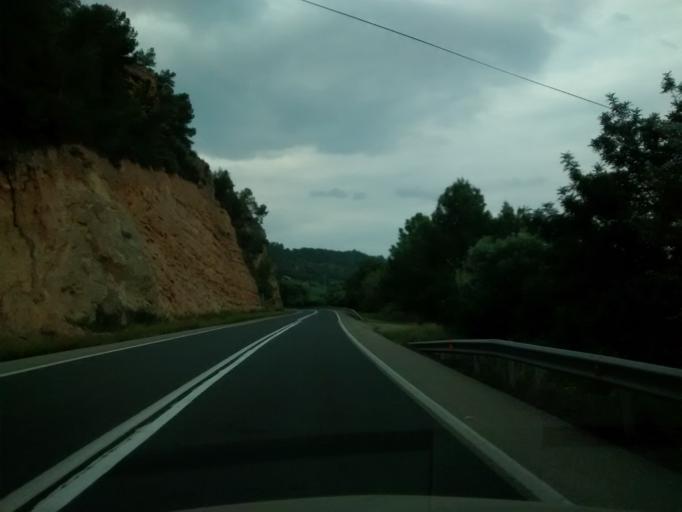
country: ES
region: Catalonia
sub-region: Provincia de Tarragona
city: Benifallet
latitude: 40.9671
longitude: 0.5097
